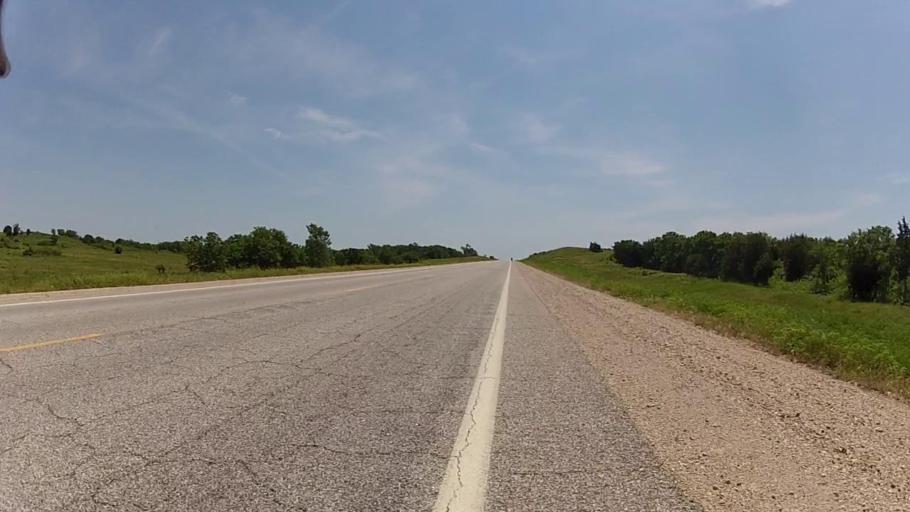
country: US
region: Kansas
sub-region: Chautauqua County
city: Sedan
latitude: 37.1131
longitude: -96.4481
